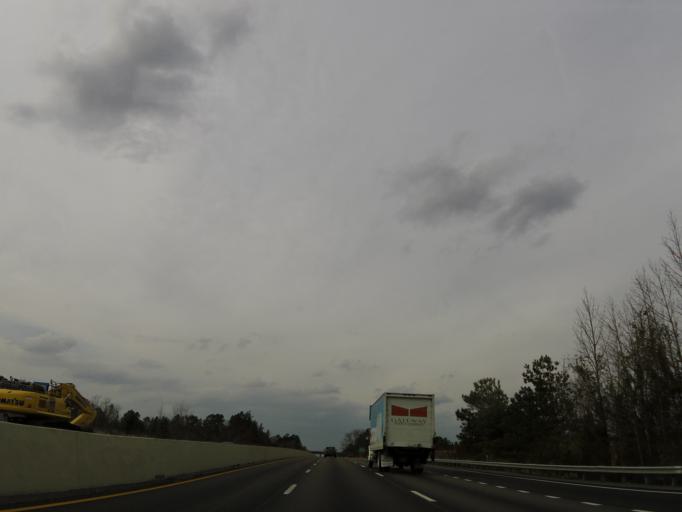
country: US
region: South Carolina
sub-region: Calhoun County
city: Oak Grove
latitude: 33.8076
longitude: -81.0048
